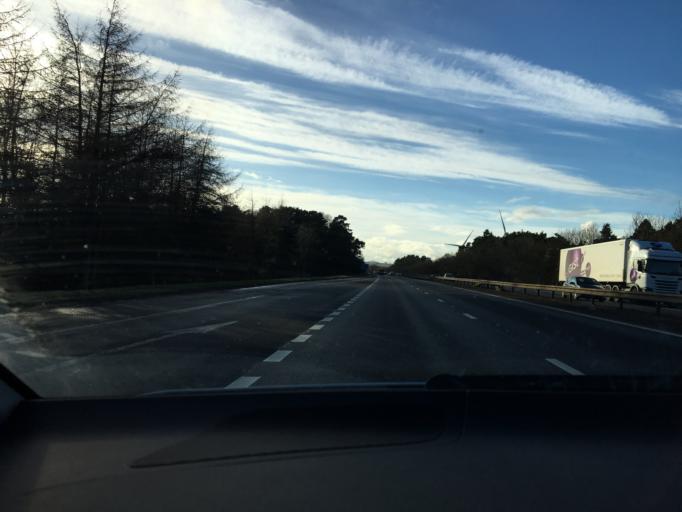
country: GB
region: Scotland
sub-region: West Lothian
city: Armadale
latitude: 55.8702
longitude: -3.7131
